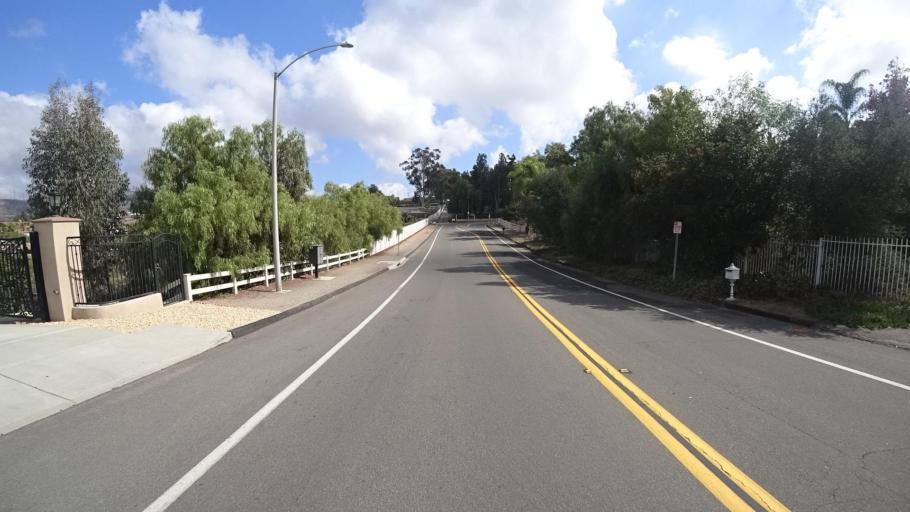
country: US
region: California
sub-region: San Diego County
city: Granite Hills
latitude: 32.7804
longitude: -116.9038
